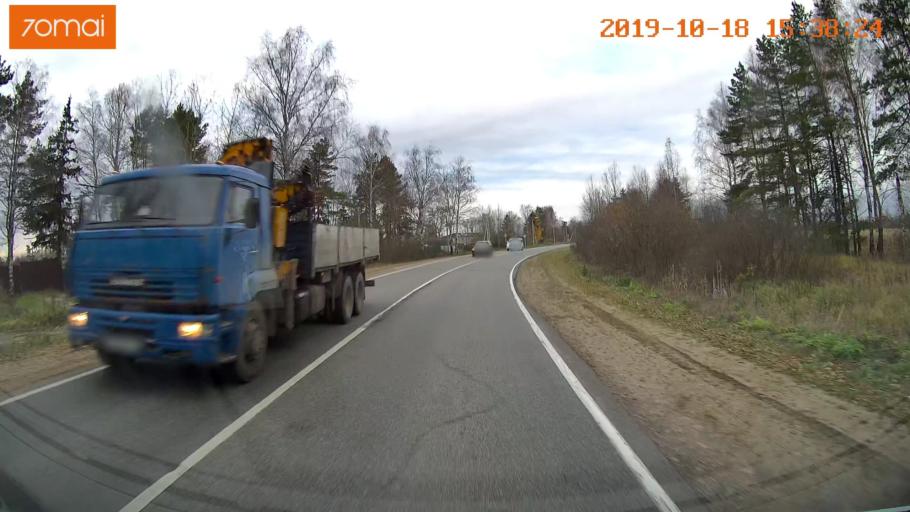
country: RU
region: Vladimir
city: Golovino
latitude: 55.9107
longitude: 40.6072
